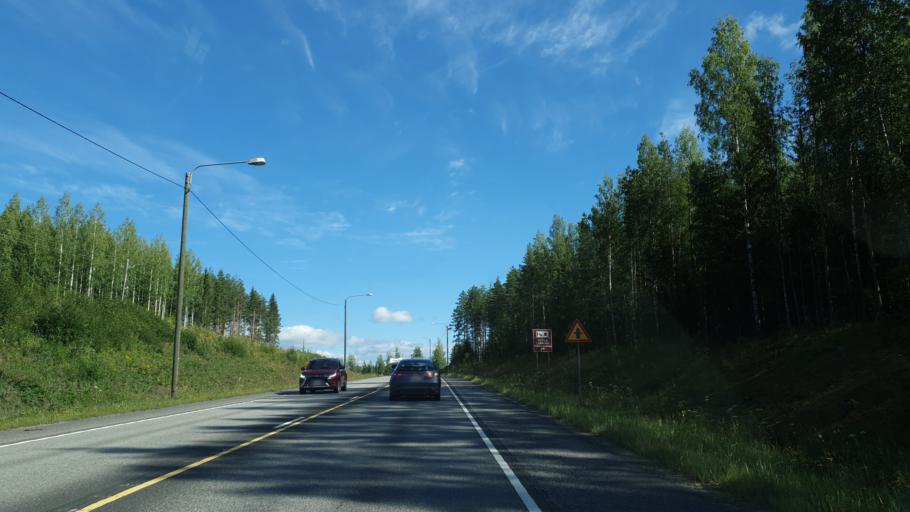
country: FI
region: Central Finland
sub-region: Jyvaeskylae
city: Toivakka
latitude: 62.2472
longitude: 26.0328
